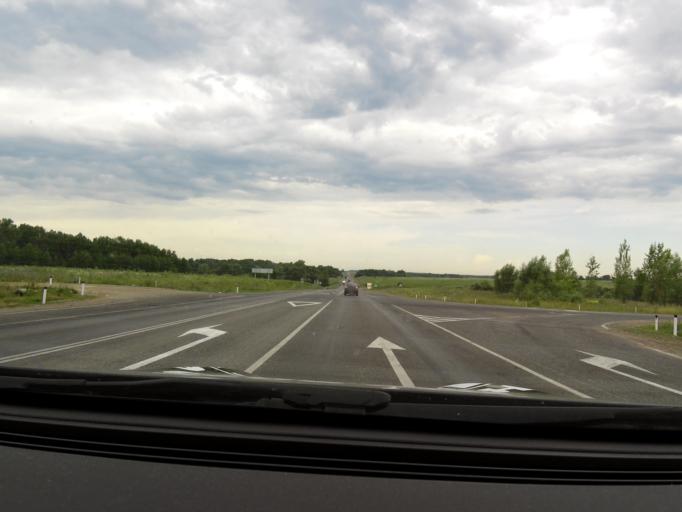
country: RU
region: Bashkortostan
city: Kudeyevskiy
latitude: 54.8172
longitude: 56.7946
